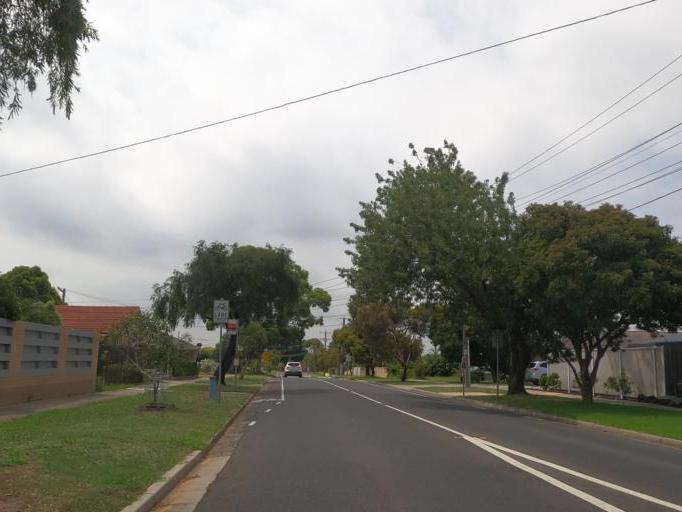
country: AU
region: Victoria
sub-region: Hume
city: Gladstone Park
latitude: -37.6850
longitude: 144.8871
